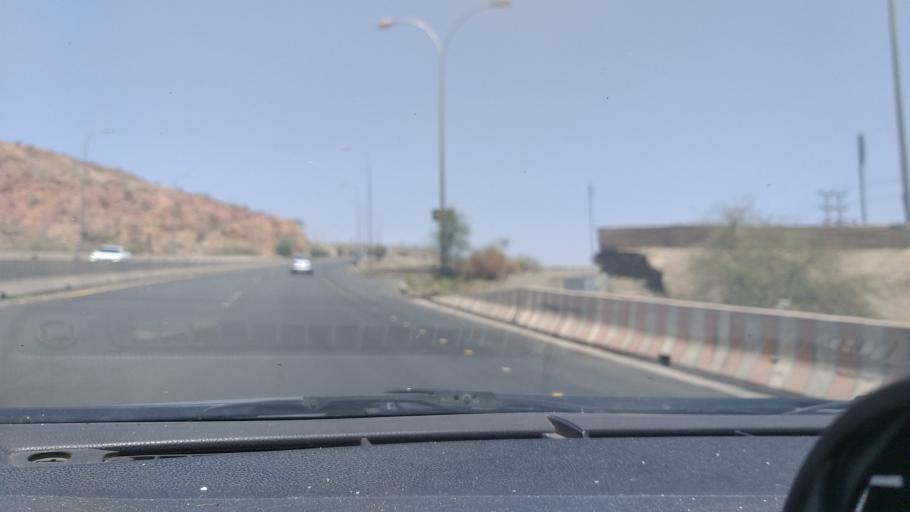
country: SA
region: Makkah
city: Al Hada
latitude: 21.3499
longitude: 40.3128
